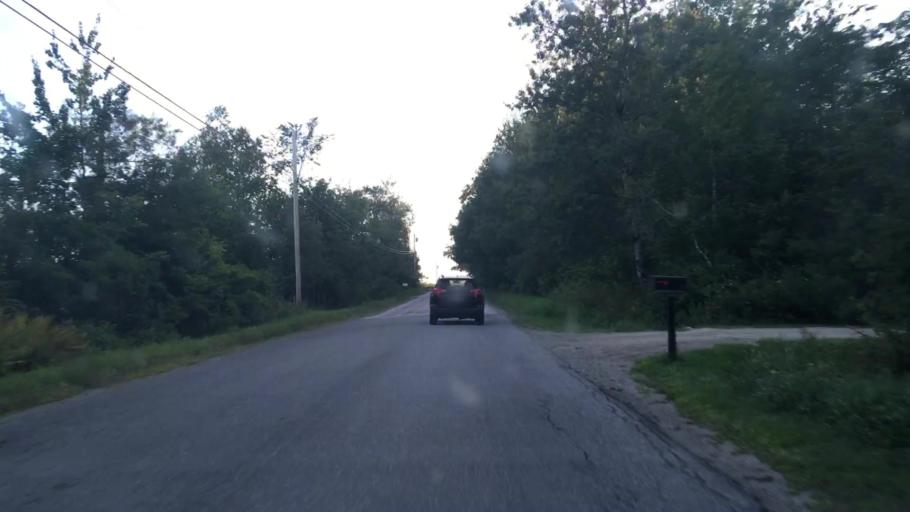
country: US
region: Maine
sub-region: Waldo County
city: Frankfort
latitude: 44.6789
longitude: -68.9150
